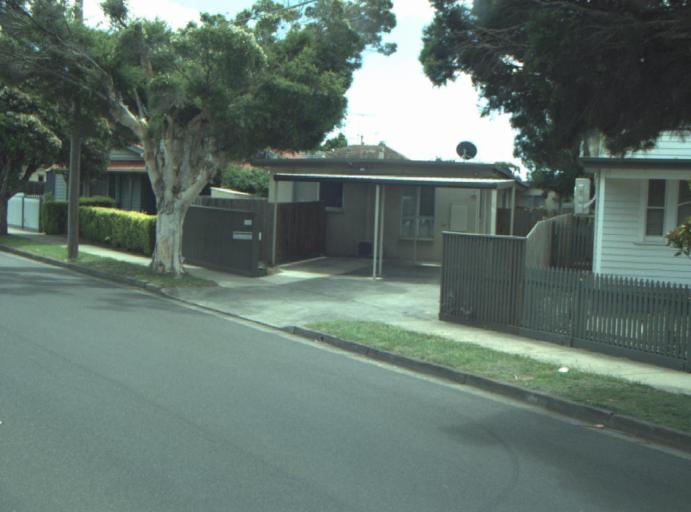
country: AU
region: Victoria
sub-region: Greater Geelong
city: Breakwater
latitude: -38.1781
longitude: 144.3450
